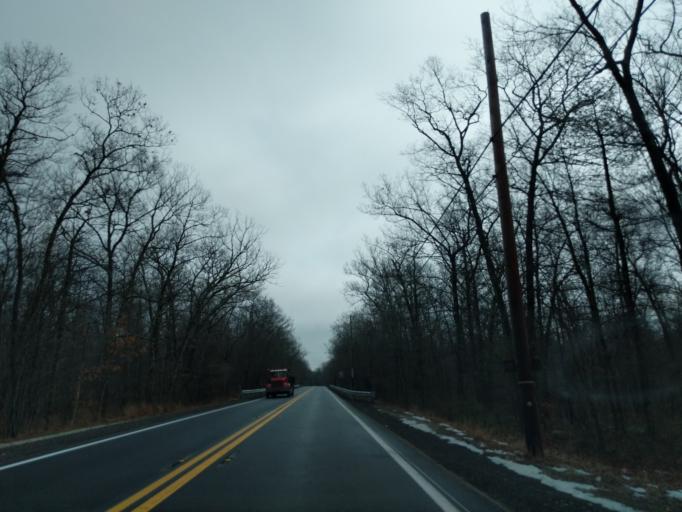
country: US
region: Massachusetts
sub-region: Worcester County
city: Douglas
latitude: 42.0560
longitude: -71.7860
